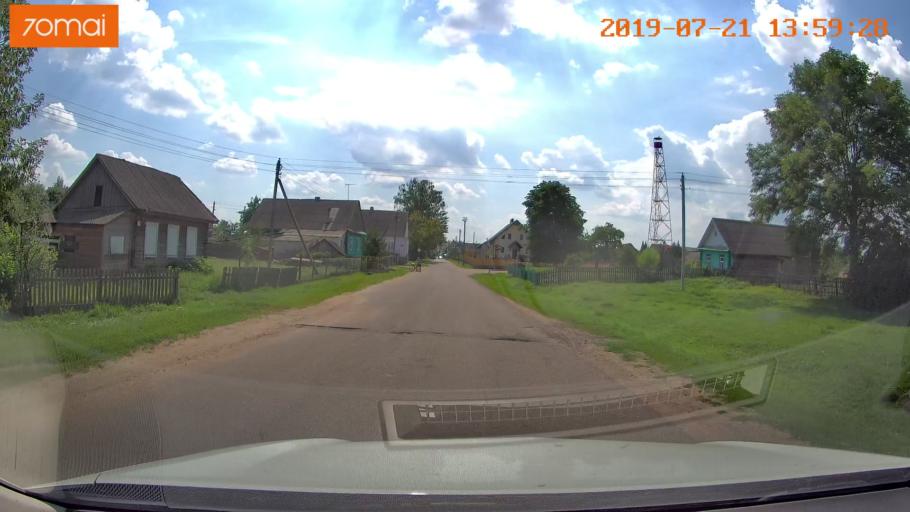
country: BY
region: Grodnenskaya
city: Lyubcha
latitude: 53.7538
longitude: 26.0641
